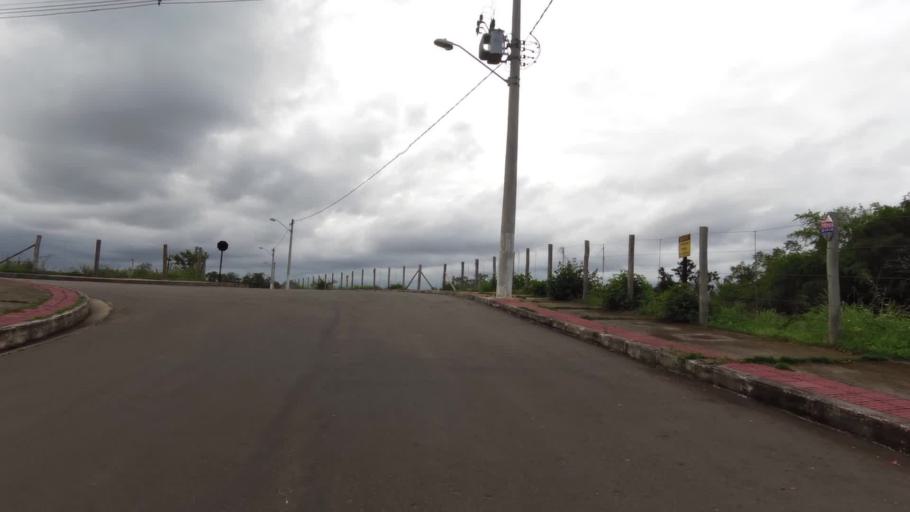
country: BR
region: Espirito Santo
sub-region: Piuma
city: Piuma
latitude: -20.8002
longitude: -40.6467
